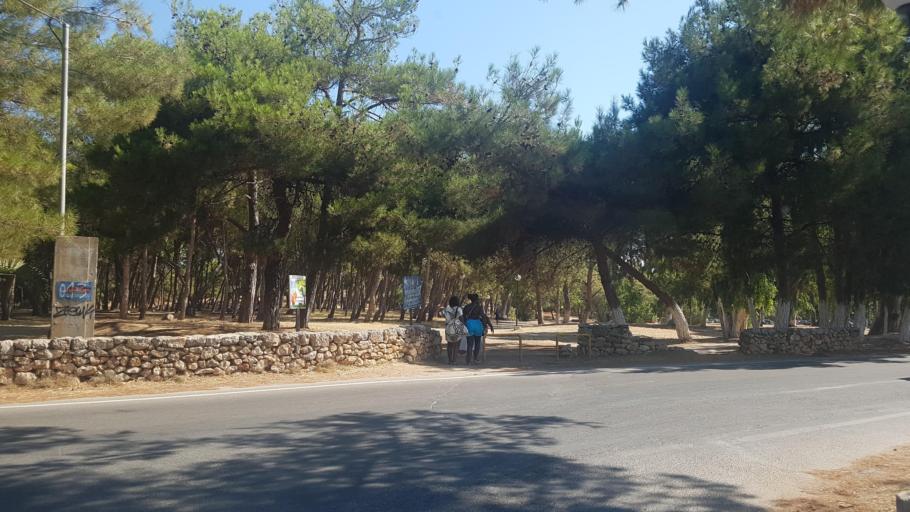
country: GR
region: Crete
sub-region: Nomos Chanias
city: Daratsos
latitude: 35.5124
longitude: 23.9801
